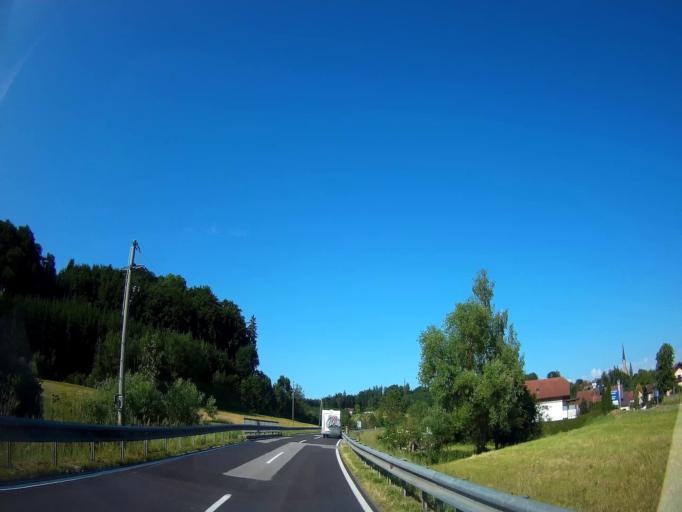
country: AT
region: Salzburg
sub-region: Politischer Bezirk Salzburg-Umgebung
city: Dorfbeuern
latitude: 48.1259
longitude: 13.0085
